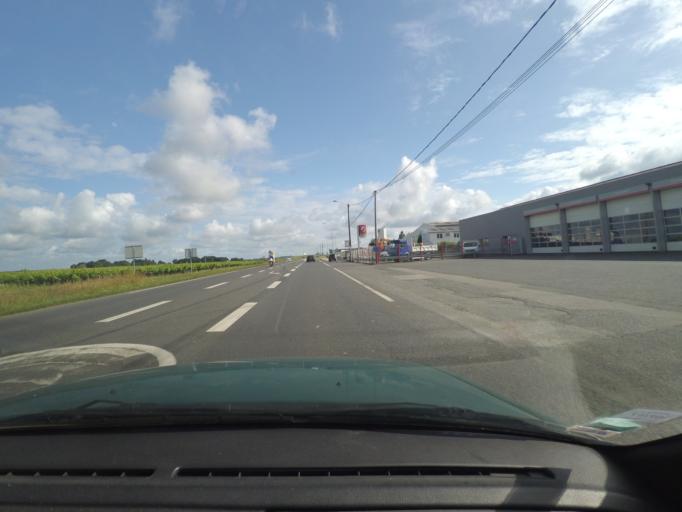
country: FR
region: Pays de la Loire
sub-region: Departement de la Loire-Atlantique
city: Mouzillon
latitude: 47.1240
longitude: -1.2826
